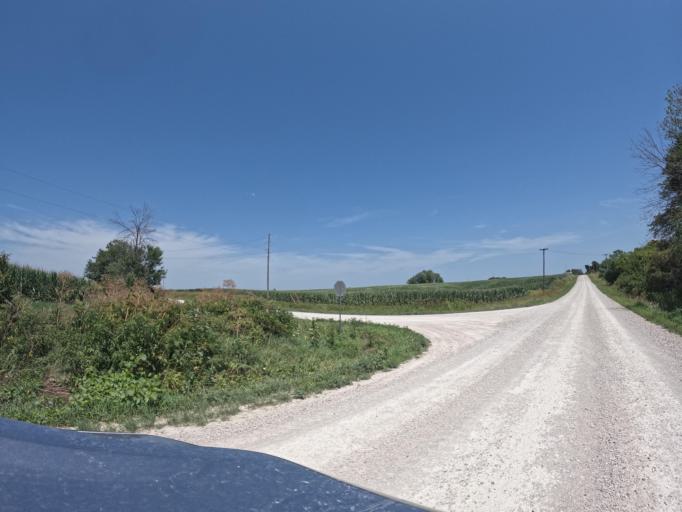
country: US
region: Iowa
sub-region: Henry County
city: Mount Pleasant
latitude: 40.9449
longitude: -91.6604
